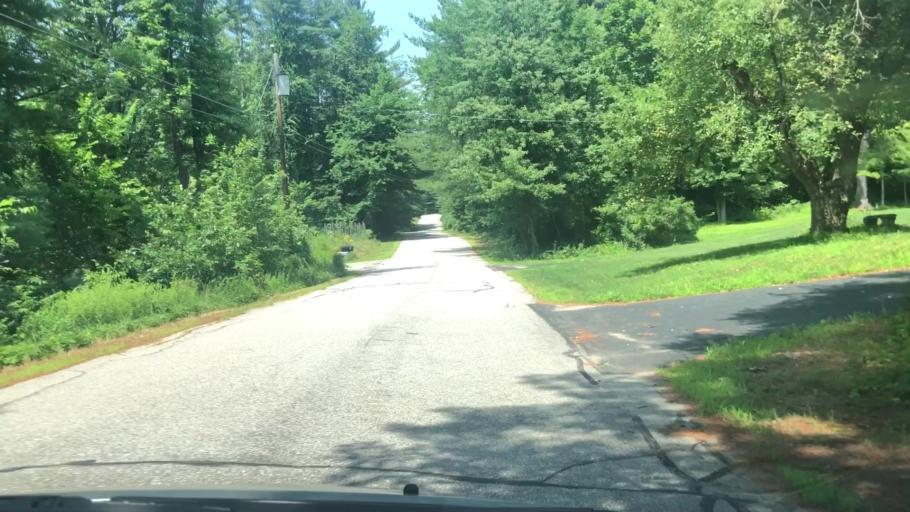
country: US
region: New Hampshire
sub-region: Hillsborough County
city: Milford
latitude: 42.8717
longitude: -71.6273
